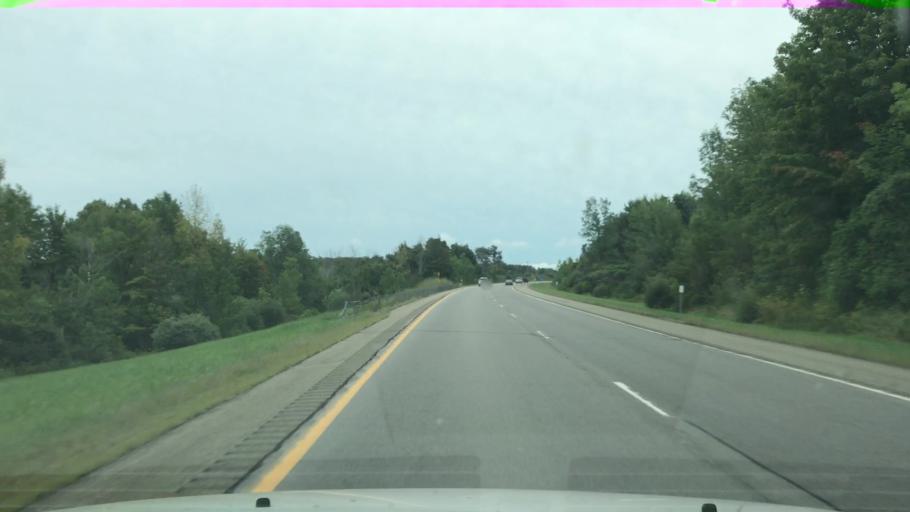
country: US
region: New York
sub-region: Erie County
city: Springville
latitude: 42.5689
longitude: -78.7142
